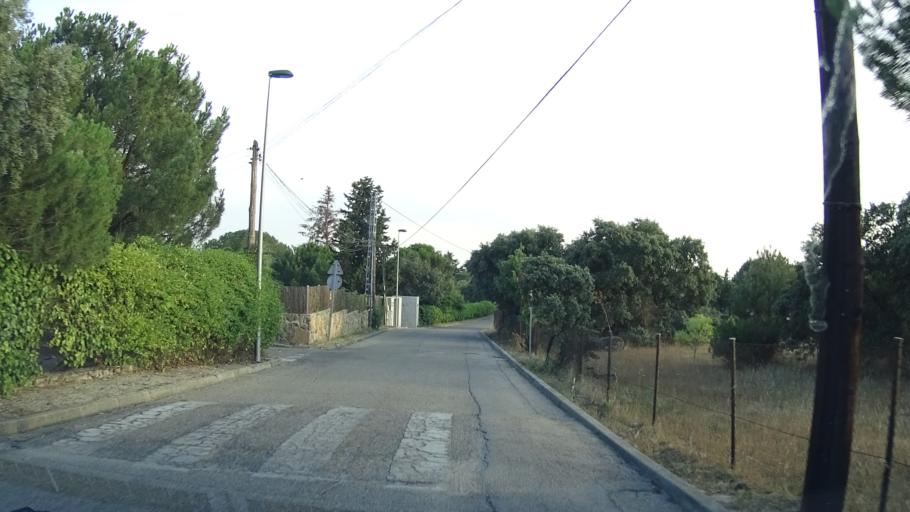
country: ES
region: Madrid
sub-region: Provincia de Madrid
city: Torrelodones
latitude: 40.5878
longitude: -3.9469
